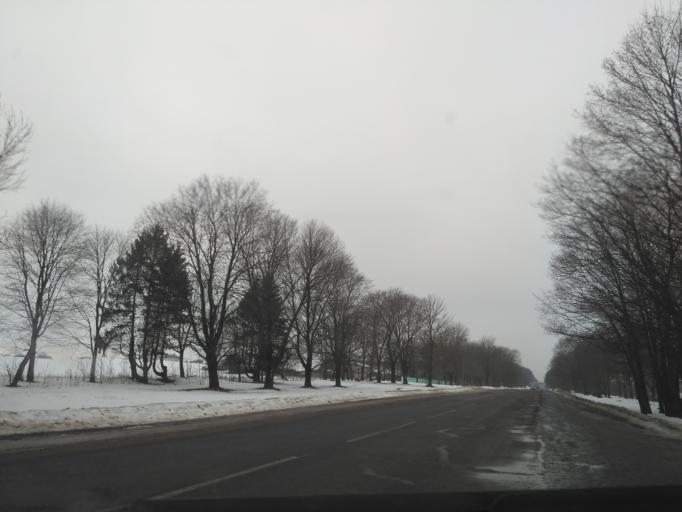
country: BY
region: Minsk
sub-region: Smalyavitski Rayon
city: Oktjabr'skij
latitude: 54.0301
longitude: 28.2133
